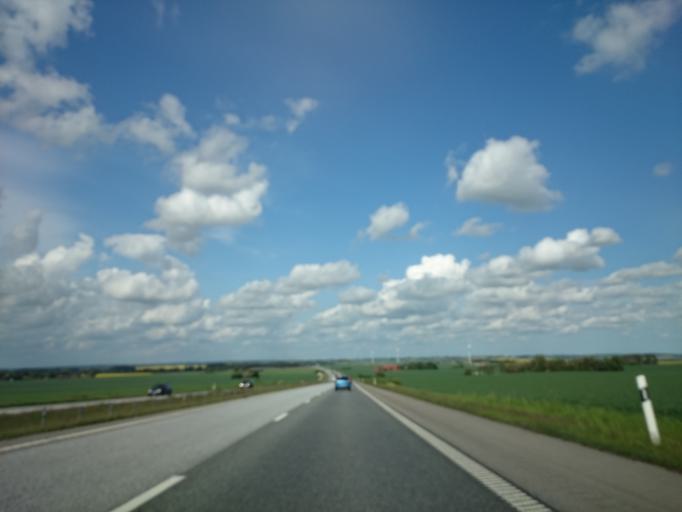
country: SE
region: Skane
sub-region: Lunds Kommun
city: Lund
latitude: 55.7471
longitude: 13.2638
